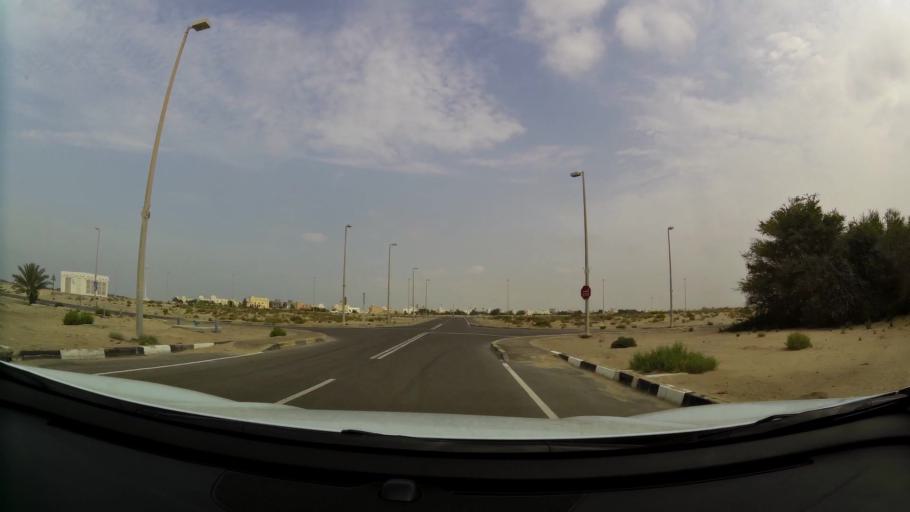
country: AE
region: Abu Dhabi
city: Abu Dhabi
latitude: 24.6367
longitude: 54.6714
